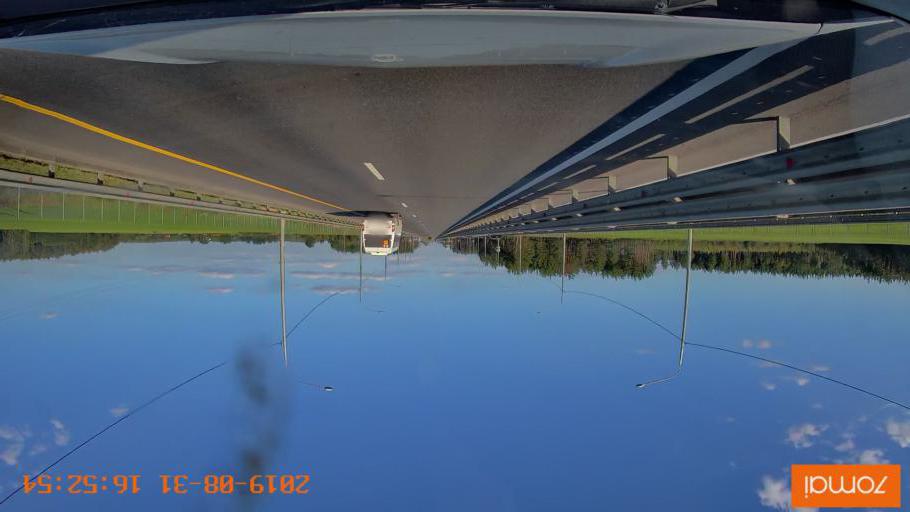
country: RU
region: Kaluga
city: Detchino
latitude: 54.7480
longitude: 36.2009
